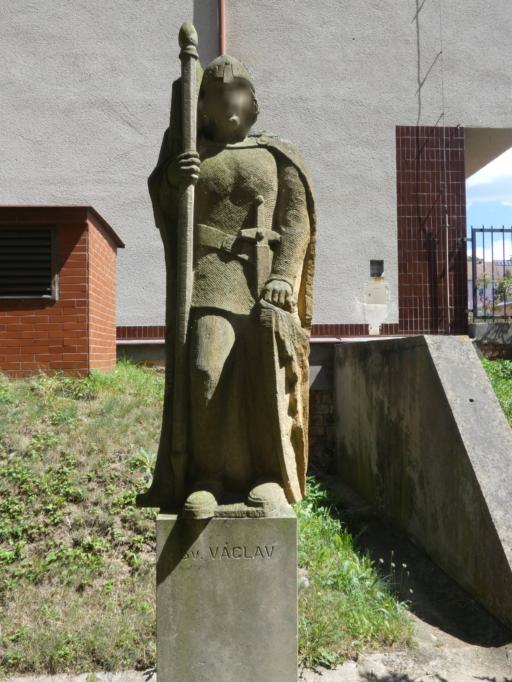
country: CZ
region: Plzensky
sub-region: Okres Plzen-Jih
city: Nepomuk
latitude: 49.4854
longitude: 13.5810
